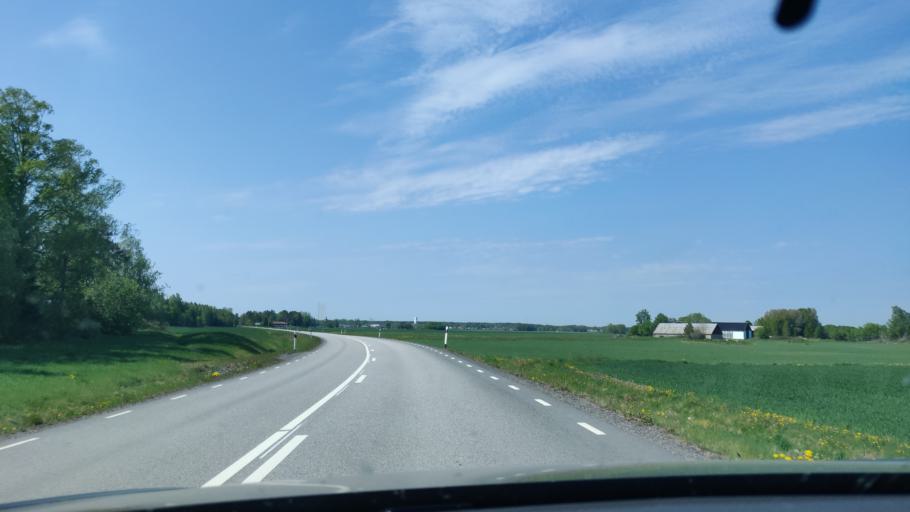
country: SE
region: Uppsala
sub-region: Heby Kommun
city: OEstervala
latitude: 60.1605
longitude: 17.2043
